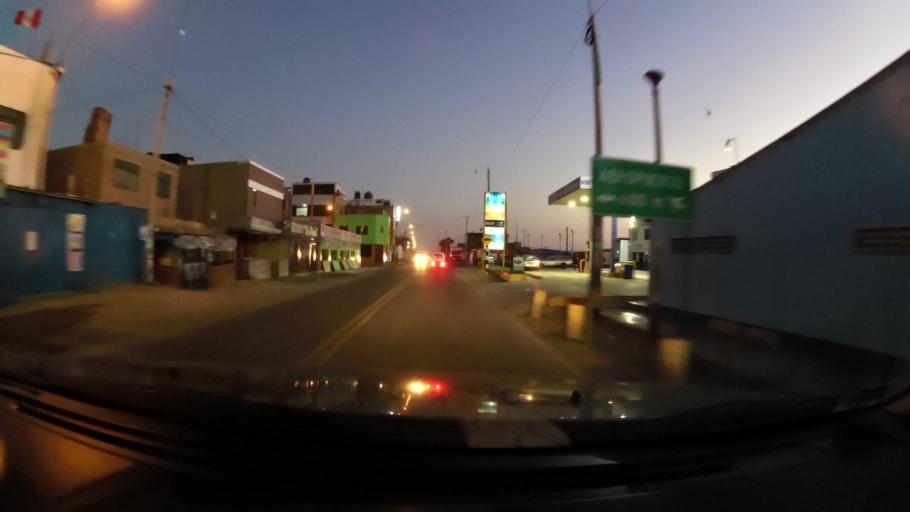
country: PE
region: Ica
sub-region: Provincia de Pisco
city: Pisco
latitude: -13.7336
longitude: -76.2244
